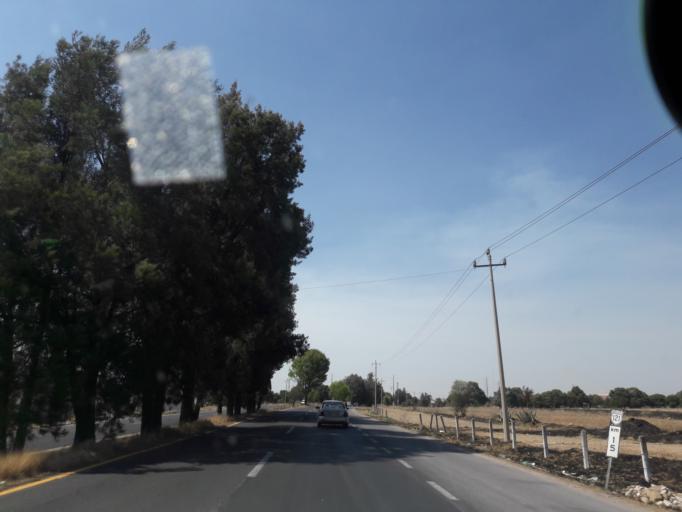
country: MX
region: Tlaxcala
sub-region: Santa Cruz Quilehtla
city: Ayometitla
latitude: 19.1956
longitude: -98.1951
